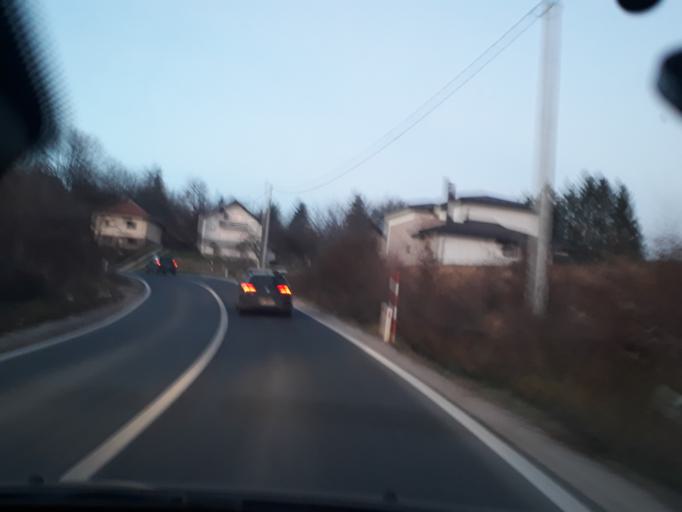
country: BA
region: Federation of Bosnia and Herzegovina
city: Hadzici
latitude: 43.8839
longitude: 18.1934
